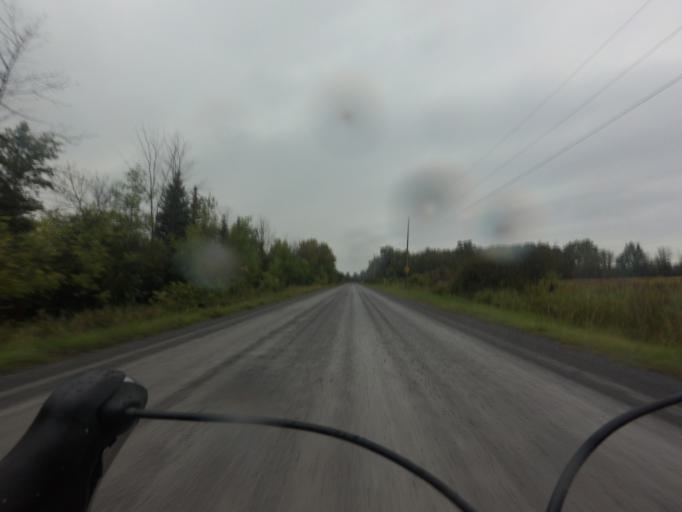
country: CA
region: Ontario
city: Bells Corners
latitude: 45.1876
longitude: -75.7179
